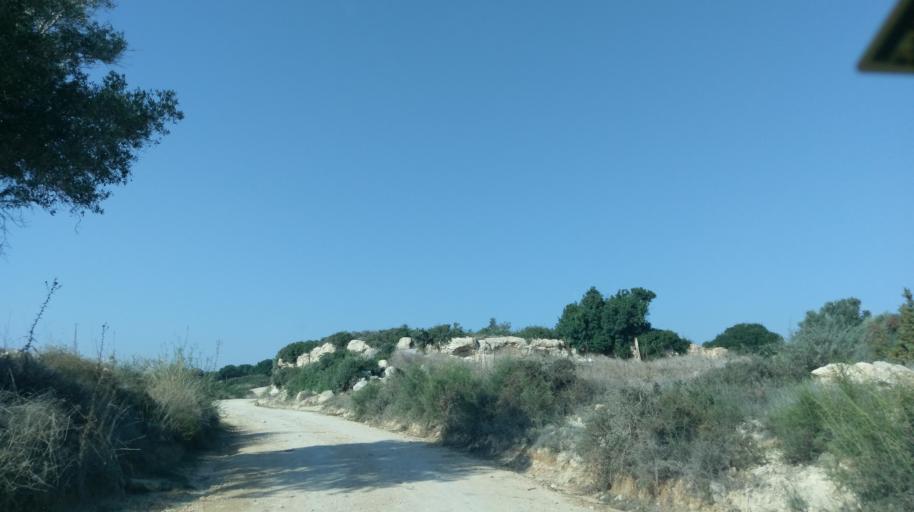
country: CY
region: Ammochostos
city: Leonarisso
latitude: 35.4859
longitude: 34.2199
